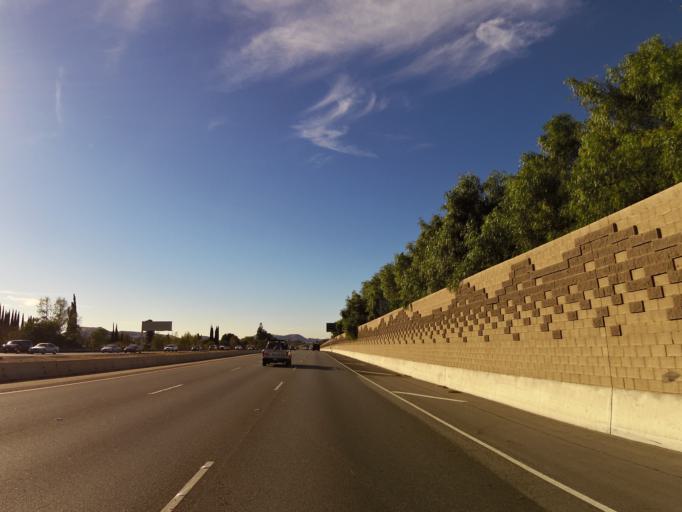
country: US
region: California
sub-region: Ventura County
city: Simi Valley
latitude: 34.2824
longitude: -118.7502
